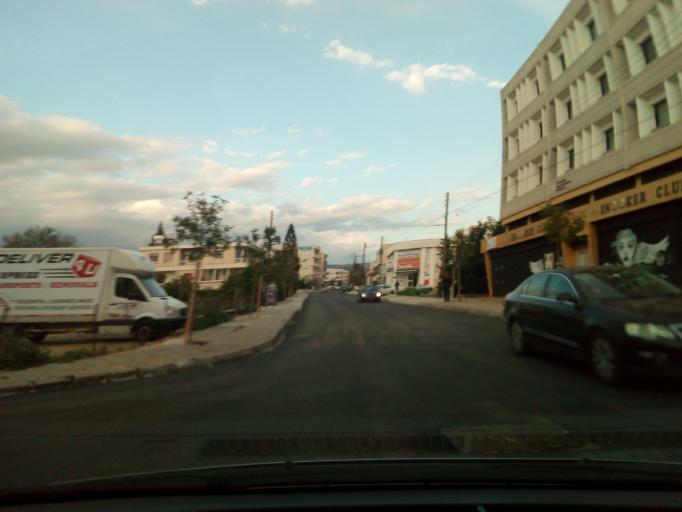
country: CY
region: Pafos
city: Paphos
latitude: 34.7780
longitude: 32.4301
